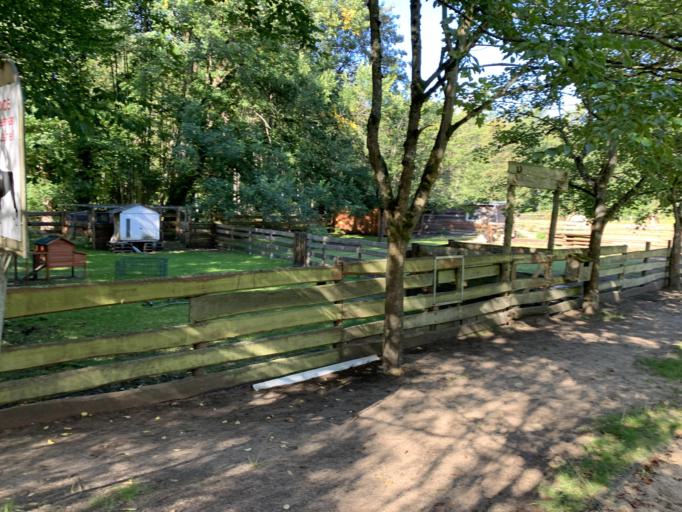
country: DE
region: Brandenburg
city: Wenzlow
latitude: 52.3487
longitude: 12.4838
